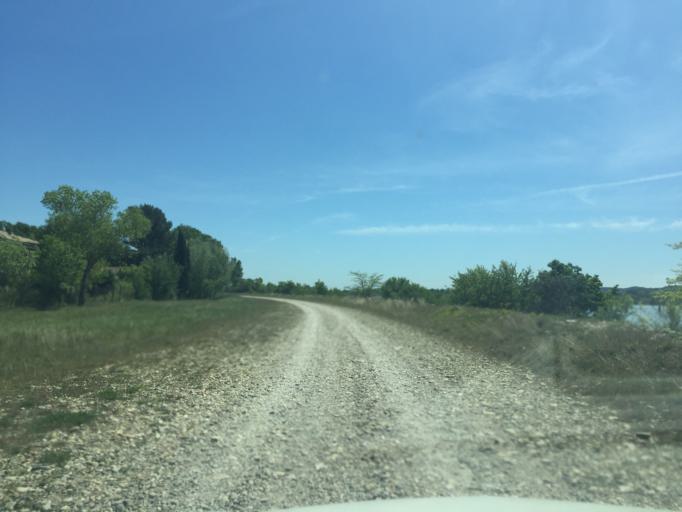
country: FR
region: Languedoc-Roussillon
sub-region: Departement du Gard
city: Roquemaure
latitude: 44.0536
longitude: 4.7911
